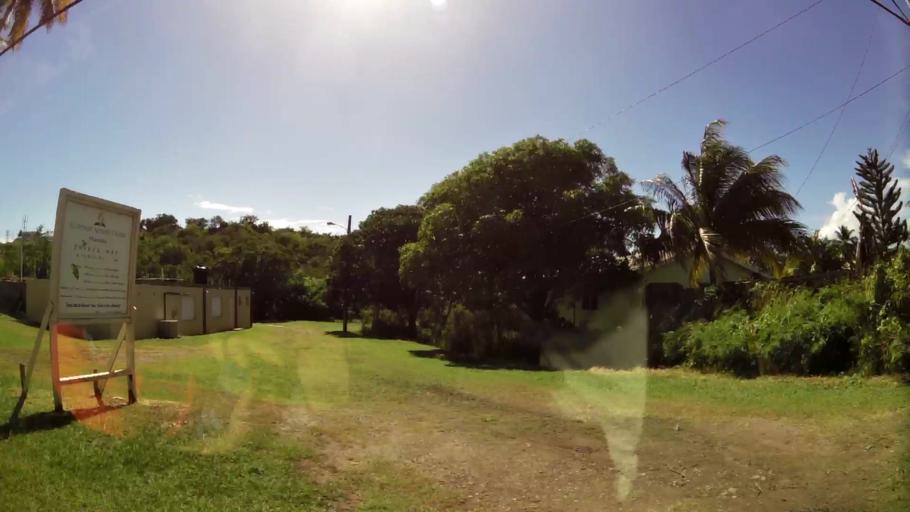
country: AG
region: Saint Paul
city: Falmouth
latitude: 17.0246
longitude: -61.7641
